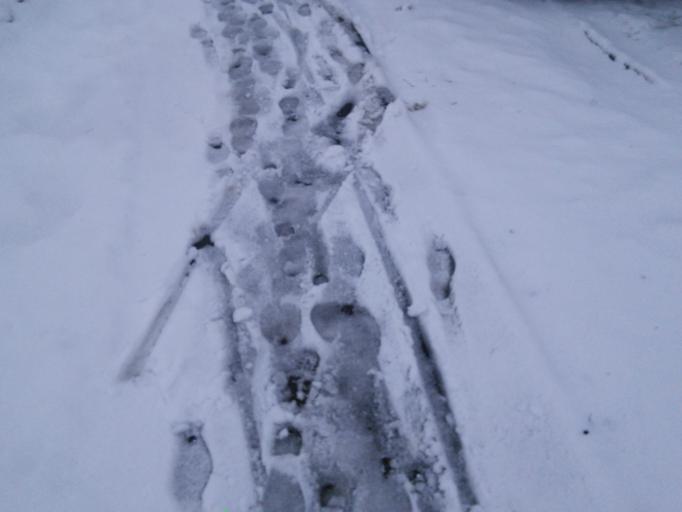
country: RU
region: Kursk
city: Chernitsyno
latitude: 51.5795
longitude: 36.0806
